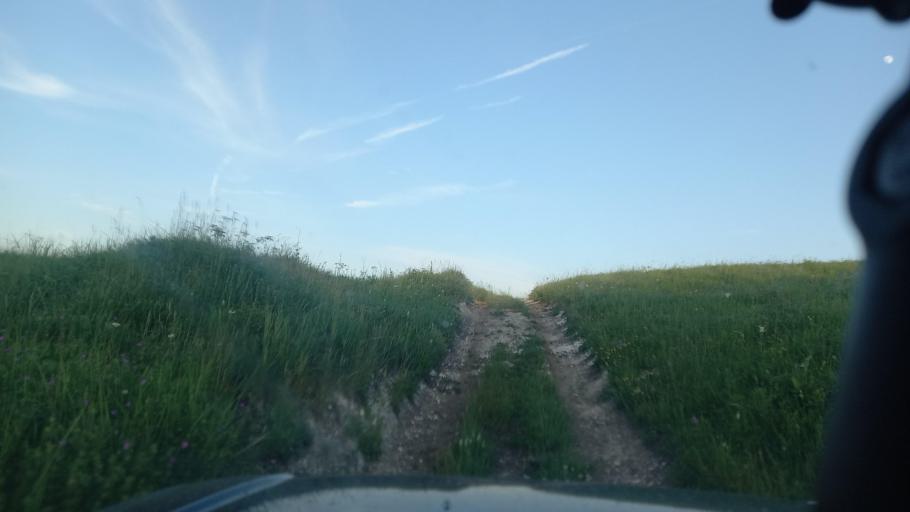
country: RU
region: Karachayevo-Cherkesiya
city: Pregradnaya
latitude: 44.1200
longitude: 41.1145
